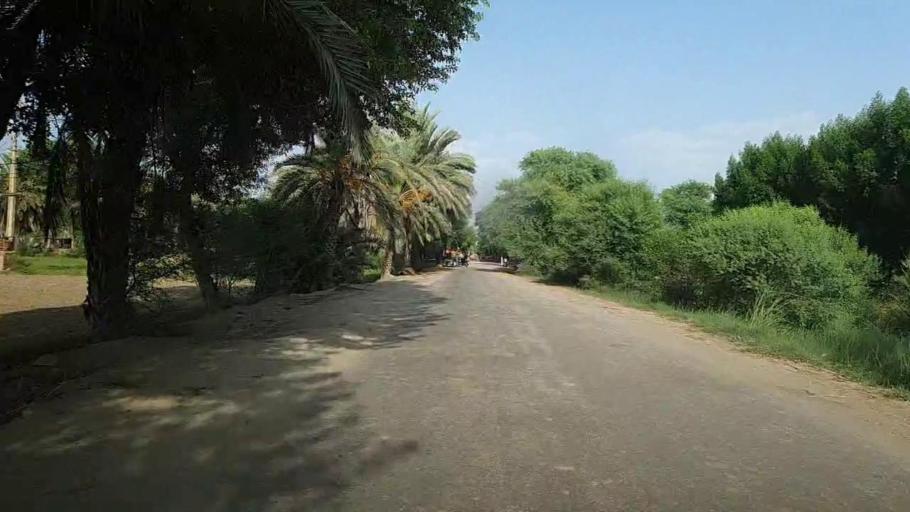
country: PK
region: Sindh
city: Khairpur
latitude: 28.0746
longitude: 69.8211
